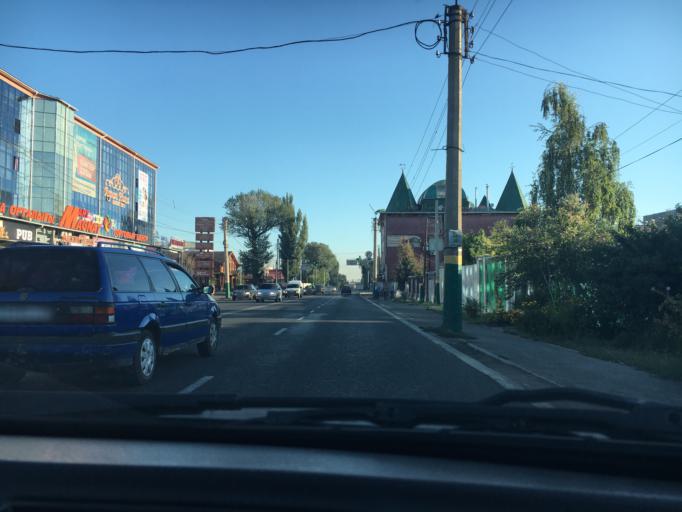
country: KZ
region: Zhambyl
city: Taraz
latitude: 42.8938
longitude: 71.3606
